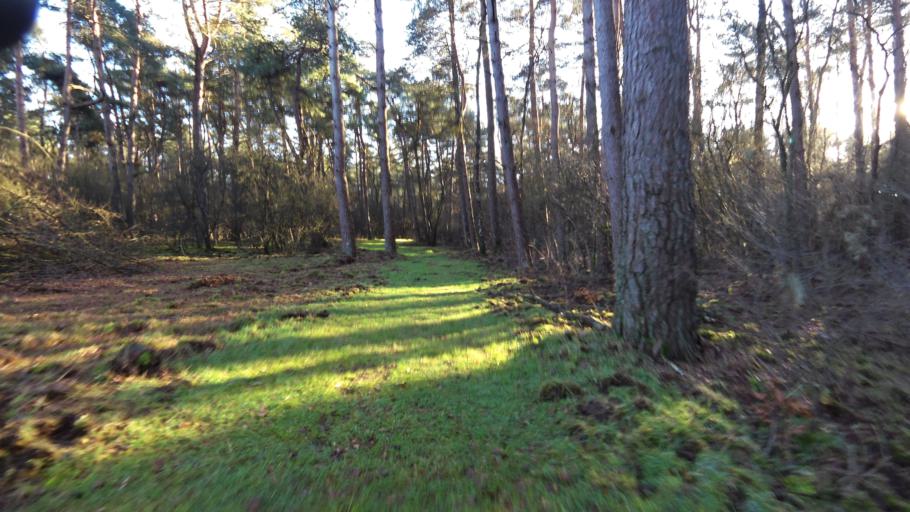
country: NL
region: Gelderland
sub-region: Gemeente Barneveld
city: Garderen
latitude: 52.2123
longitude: 5.7186
